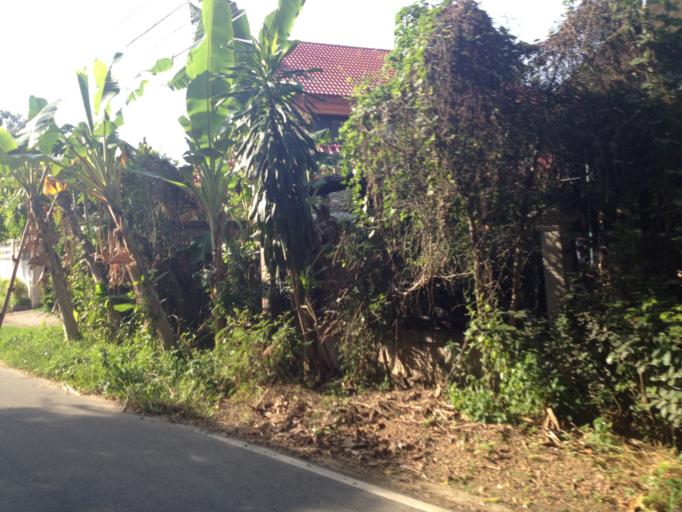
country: TH
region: Chiang Mai
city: Chiang Mai
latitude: 18.7440
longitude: 98.9525
